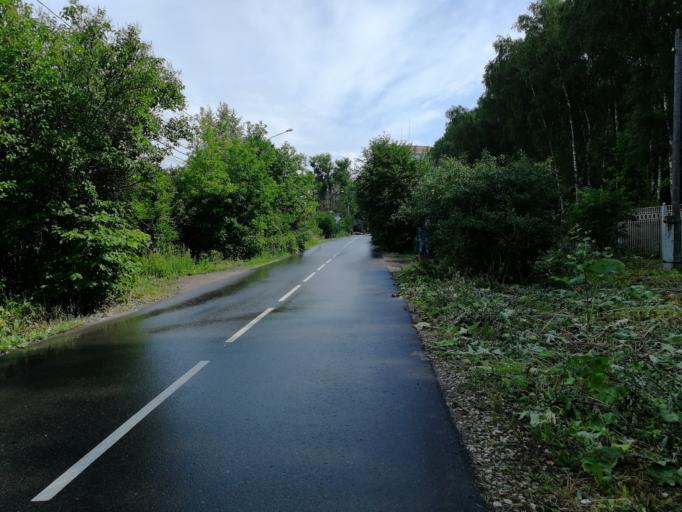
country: RU
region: Tula
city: Tula
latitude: 54.1868
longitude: 37.5837
